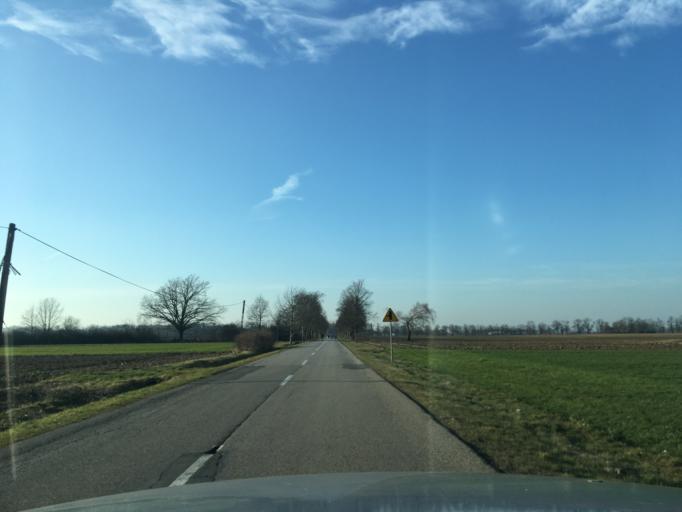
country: PL
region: Masovian Voivodeship
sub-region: Powiat pruszkowski
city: Nadarzyn
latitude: 52.0441
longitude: 20.8016
